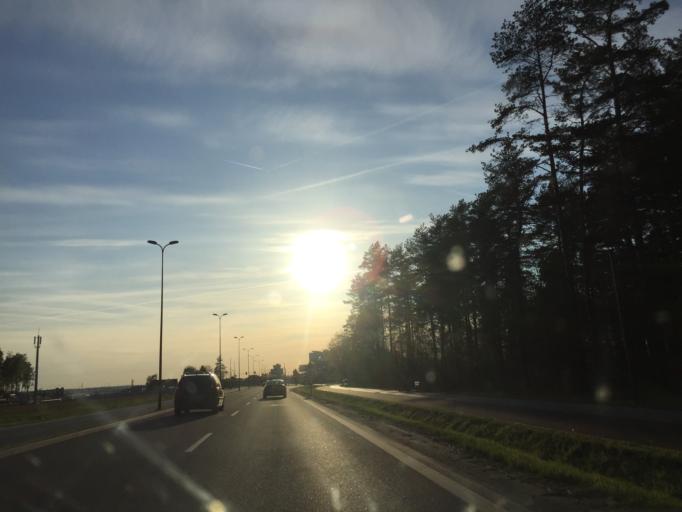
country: PL
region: Pomeranian Voivodeship
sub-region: Powiat kartuski
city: Banino
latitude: 54.3787
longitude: 18.4914
